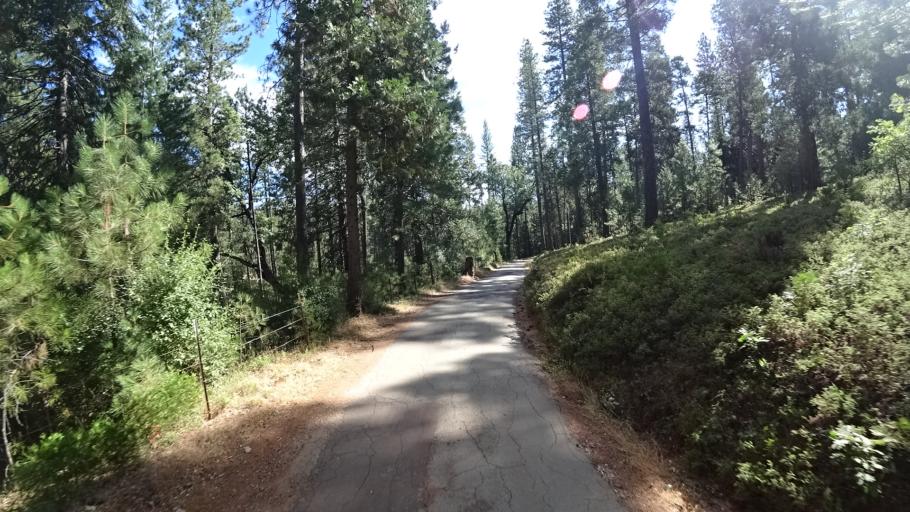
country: US
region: California
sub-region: Amador County
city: Pioneer
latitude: 38.3967
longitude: -120.4405
